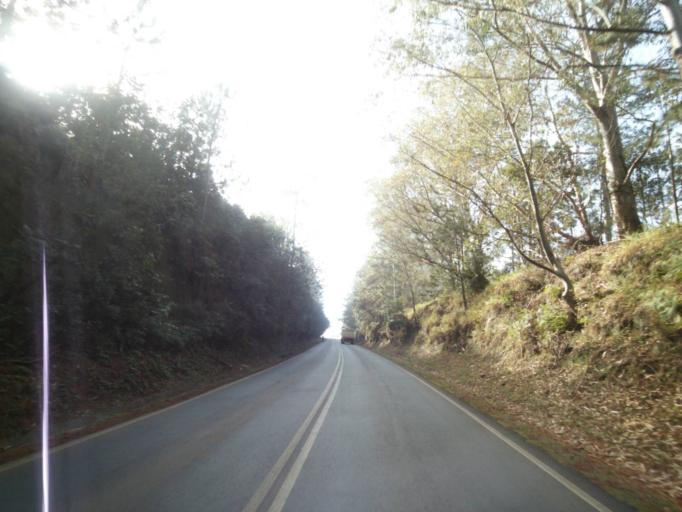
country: BR
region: Parana
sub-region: Tibagi
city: Tibagi
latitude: -24.5283
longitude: -50.3886
